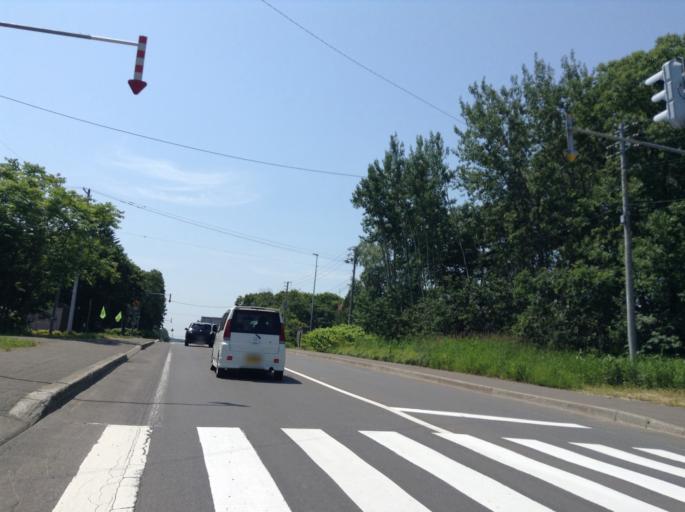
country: JP
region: Hokkaido
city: Nayoro
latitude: 44.3465
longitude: 142.4748
